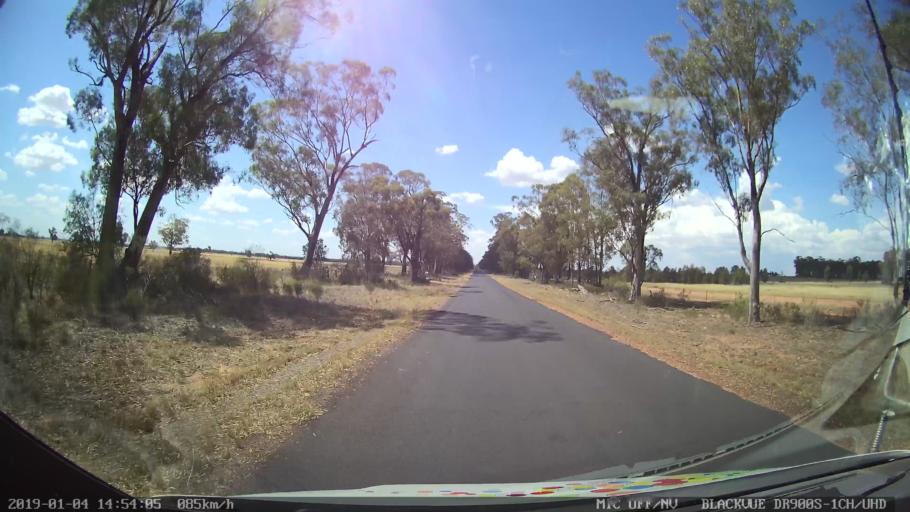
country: AU
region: New South Wales
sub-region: Dubbo Municipality
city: Dubbo
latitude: -31.9954
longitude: 148.6532
